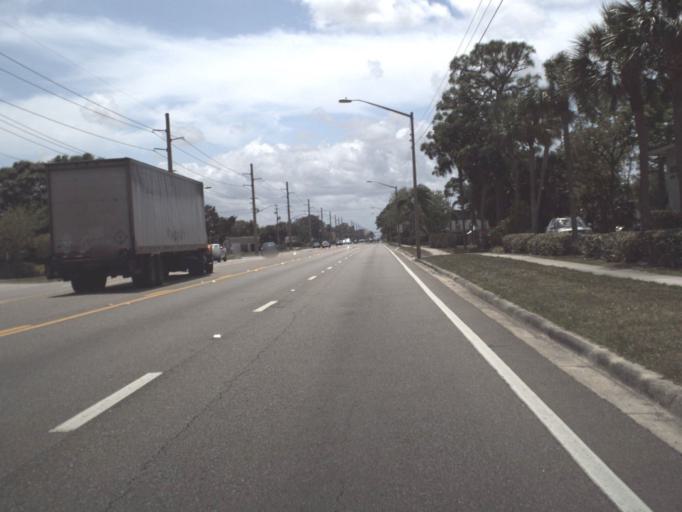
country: US
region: Florida
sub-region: Brevard County
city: Rockledge
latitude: 28.3374
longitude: -80.7426
